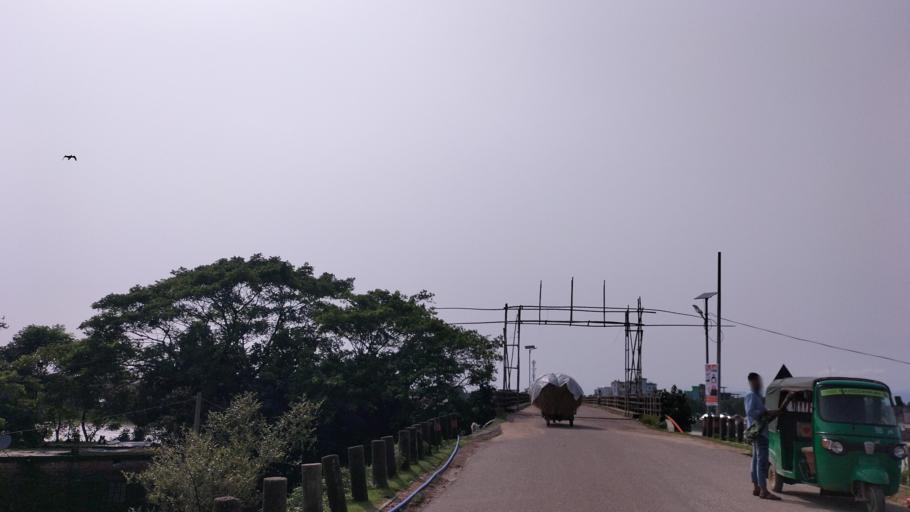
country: BD
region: Dhaka
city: Netrakona
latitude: 25.0739
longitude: 90.8915
